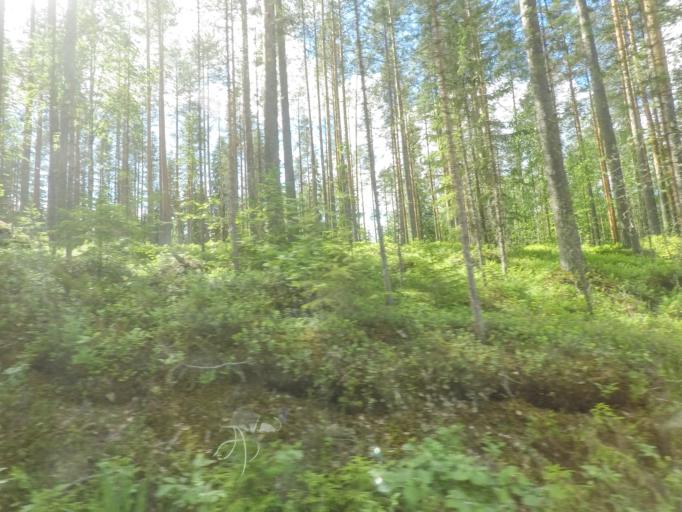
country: FI
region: Central Finland
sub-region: Jyvaeskylae
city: Hankasalmi
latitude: 62.4134
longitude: 26.6432
